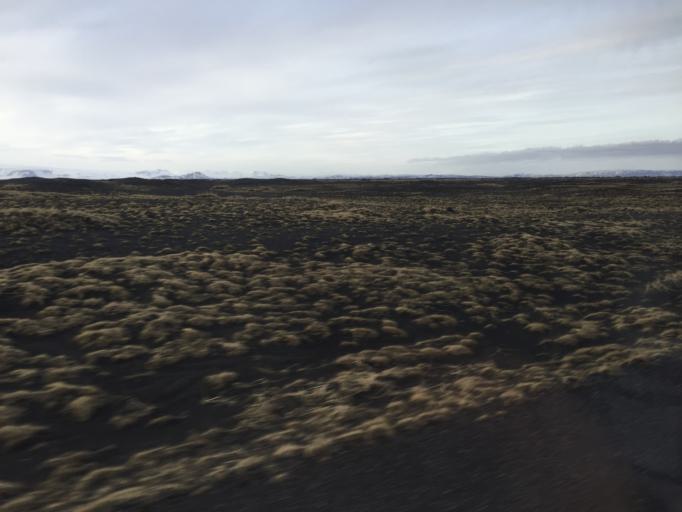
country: IS
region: South
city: Vestmannaeyjar
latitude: 63.4994
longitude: -18.5097
